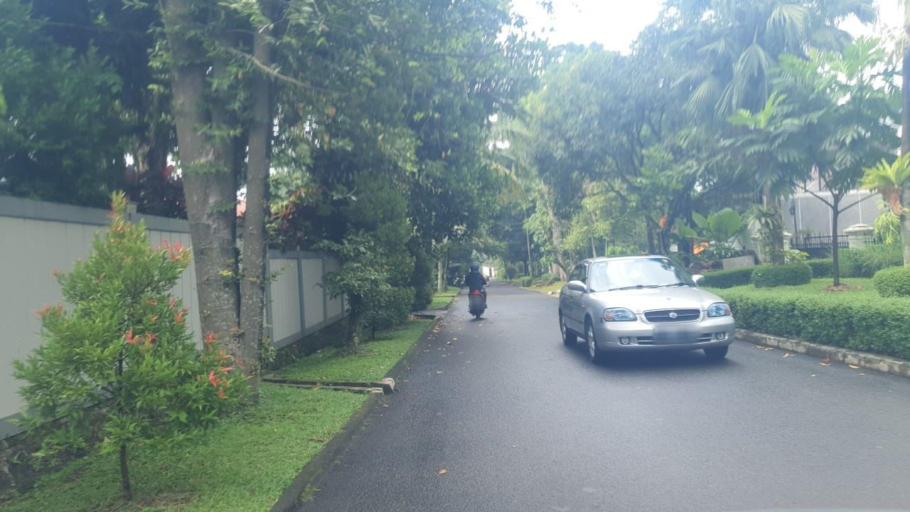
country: ID
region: West Java
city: Bogor
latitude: -6.5855
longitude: 106.8035
